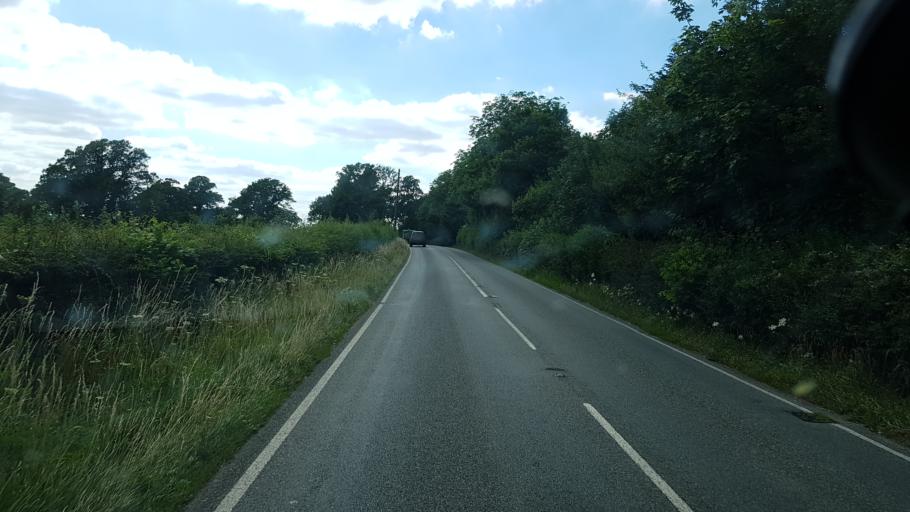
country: GB
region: England
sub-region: West Sussex
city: Southwater
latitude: 50.9958
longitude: -0.3811
